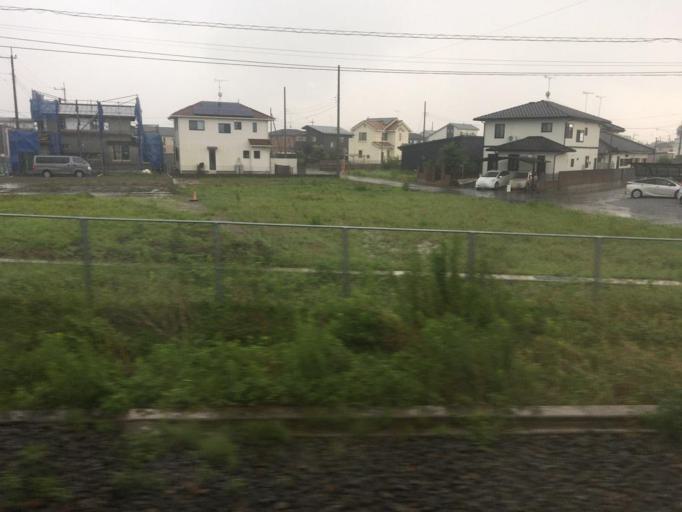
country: JP
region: Gunma
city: Tatebayashi
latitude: 36.2748
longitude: 139.4986
